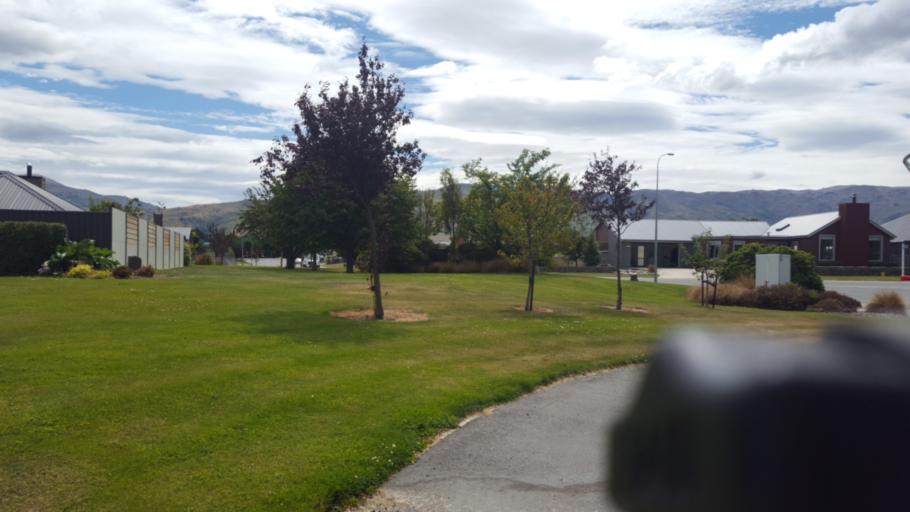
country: NZ
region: Otago
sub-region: Queenstown-Lakes District
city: Wanaka
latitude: -45.0406
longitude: 169.2179
